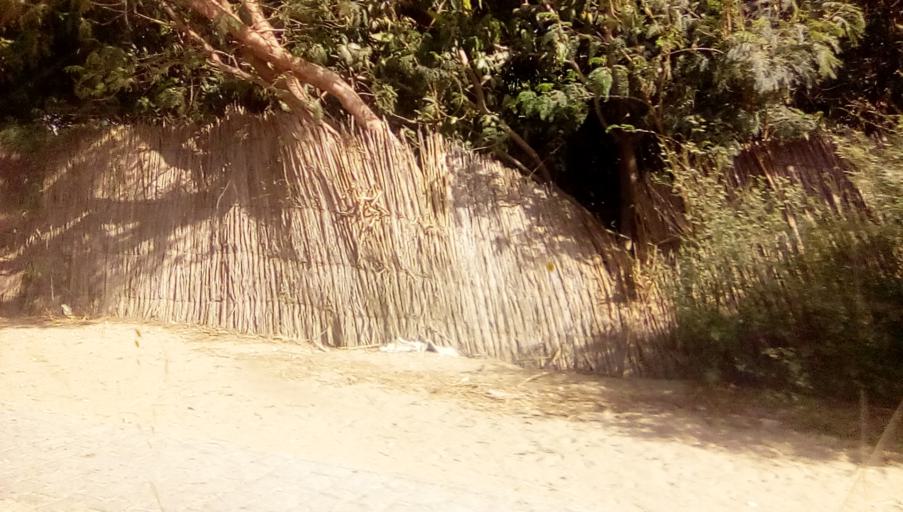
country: SN
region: Saint-Louis
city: Saint-Louis
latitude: 16.0381
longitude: -16.4598
